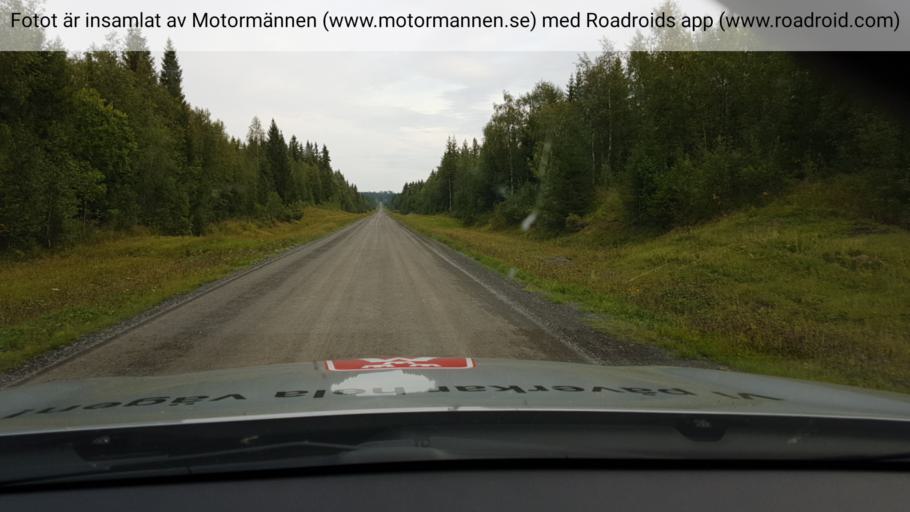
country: SE
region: Jaemtland
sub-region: OEstersunds Kommun
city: Lit
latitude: 63.6595
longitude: 14.9163
